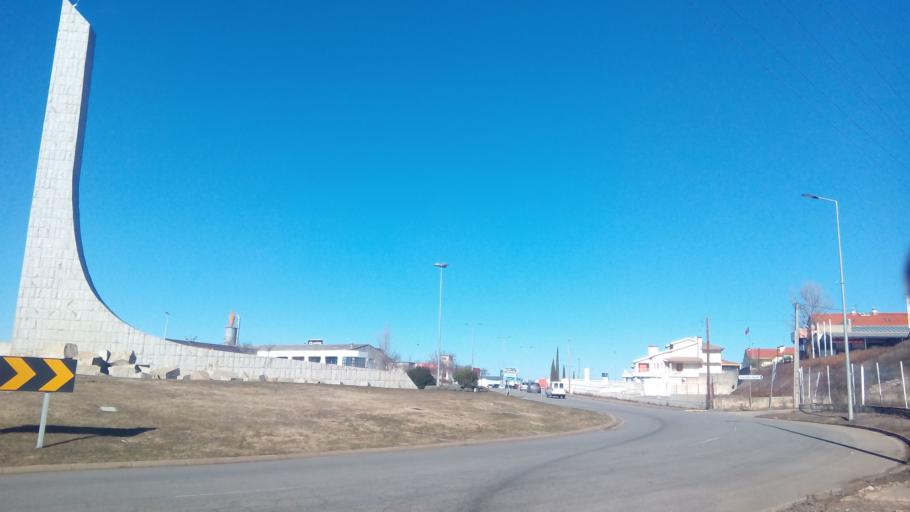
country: PT
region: Braganca
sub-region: Braganca Municipality
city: Braganca
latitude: 41.7787
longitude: -6.7790
